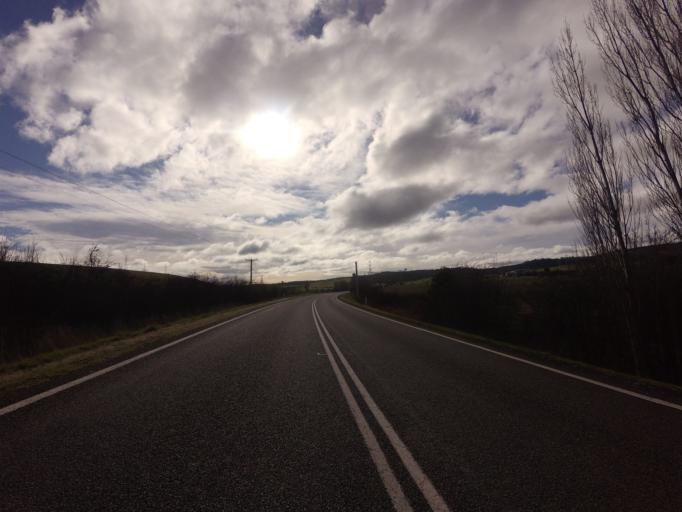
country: AU
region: Tasmania
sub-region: Derwent Valley
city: New Norfolk
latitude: -42.6669
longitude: 146.9307
